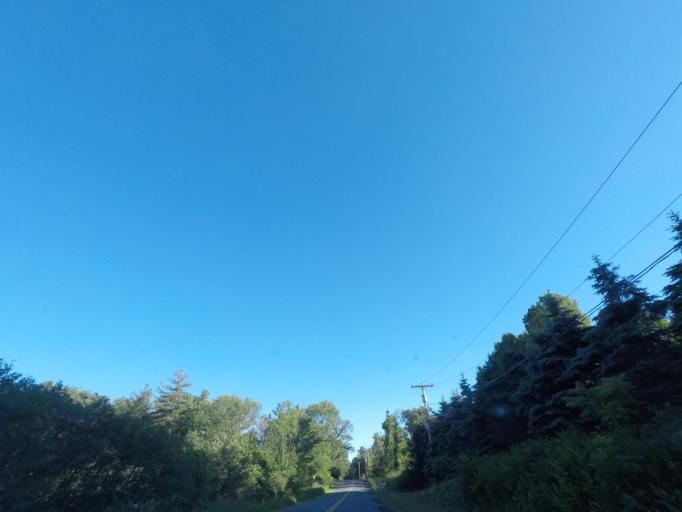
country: US
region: New York
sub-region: Rensselaer County
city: Averill Park
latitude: 42.5737
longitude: -73.5326
